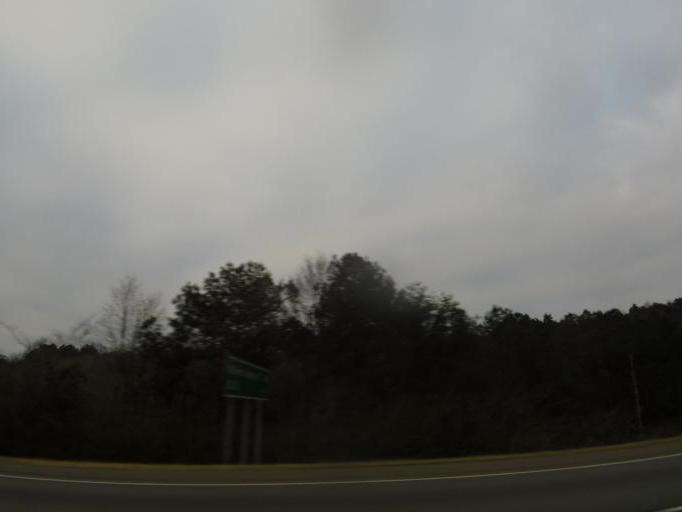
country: US
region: Alabama
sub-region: Jefferson County
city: Gardendale
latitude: 33.6362
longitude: -86.8256
